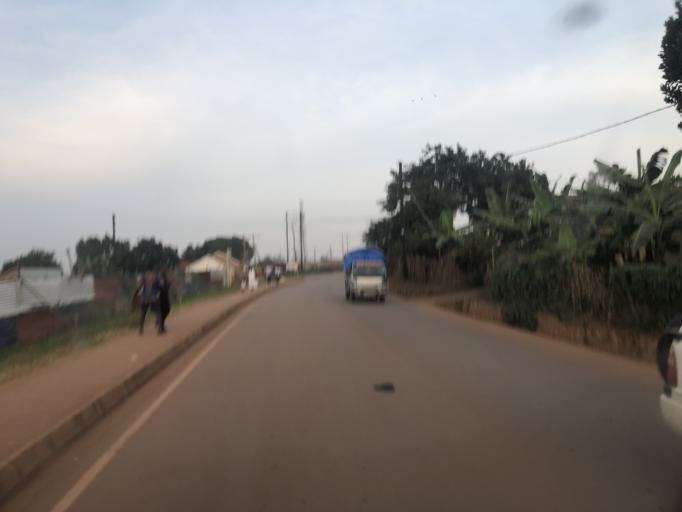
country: UG
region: Central Region
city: Kampala Central Division
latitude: 0.2923
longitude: 32.5335
